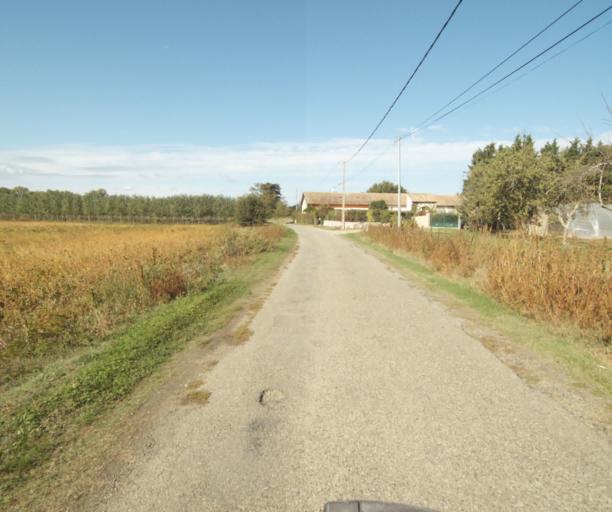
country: FR
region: Midi-Pyrenees
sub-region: Departement du Tarn-et-Garonne
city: Verdun-sur-Garonne
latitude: 43.8688
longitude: 1.2413
